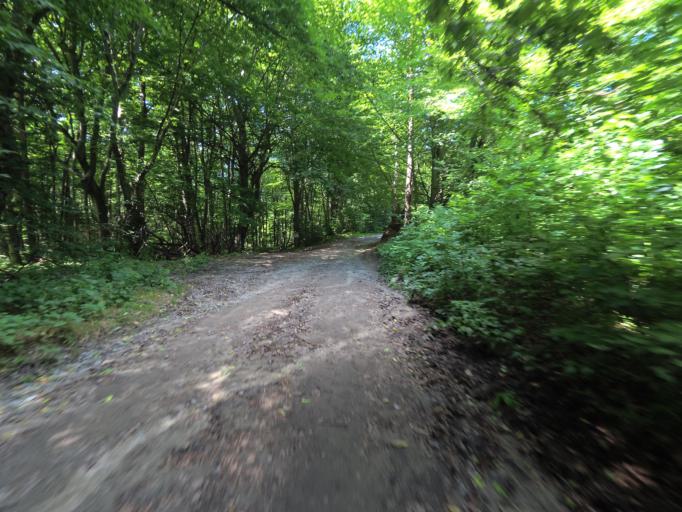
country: PL
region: Pomeranian Voivodeship
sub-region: Gdynia
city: Wielki Kack
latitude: 54.4887
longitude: 18.5017
